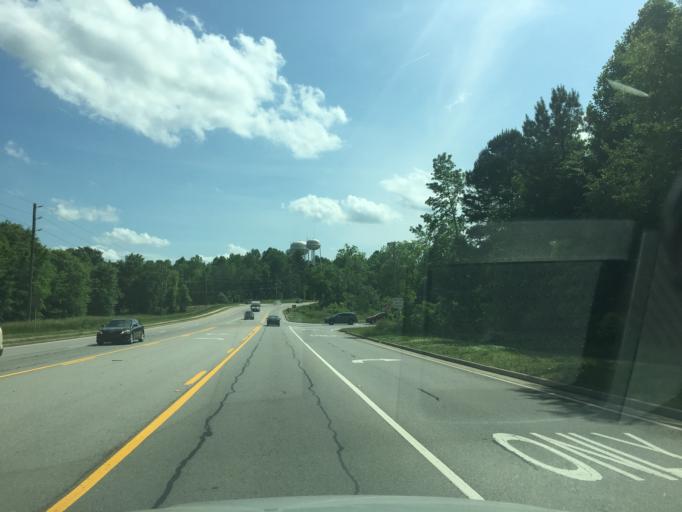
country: US
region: Georgia
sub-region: Jackson County
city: Braselton
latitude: 34.1101
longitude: -83.7658
